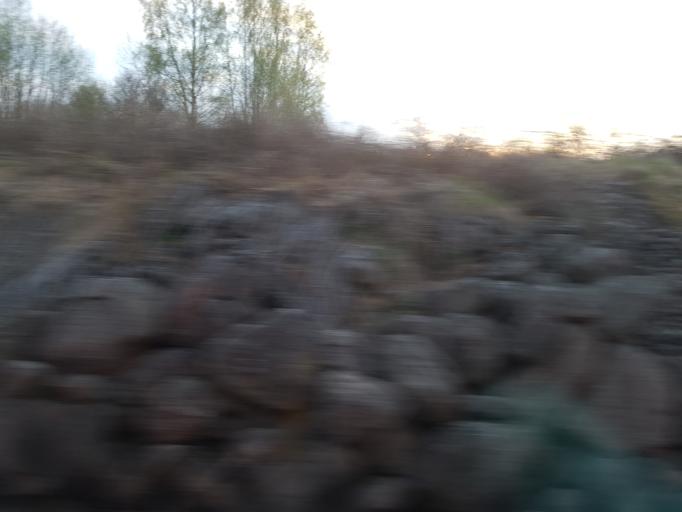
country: NO
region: Hedmark
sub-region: Hamar
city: Hamar
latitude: 60.7564
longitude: 11.1111
